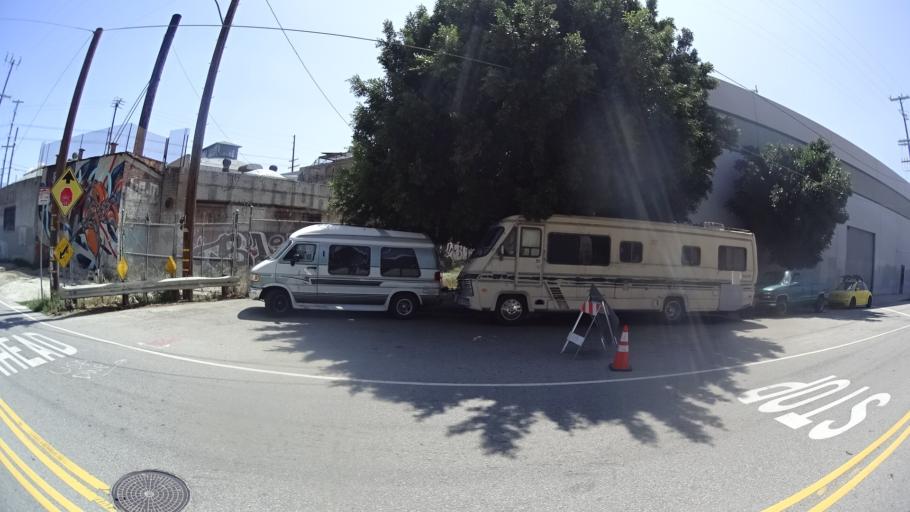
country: US
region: California
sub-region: Los Angeles County
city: Los Angeles
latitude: 34.0409
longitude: -118.2312
